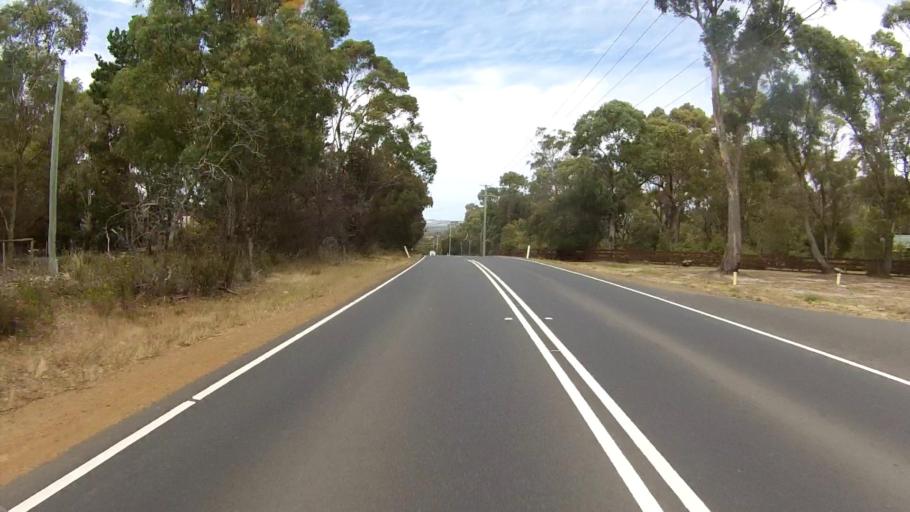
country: AU
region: Tasmania
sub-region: Clarence
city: Acton Park
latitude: -42.8810
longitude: 147.4820
